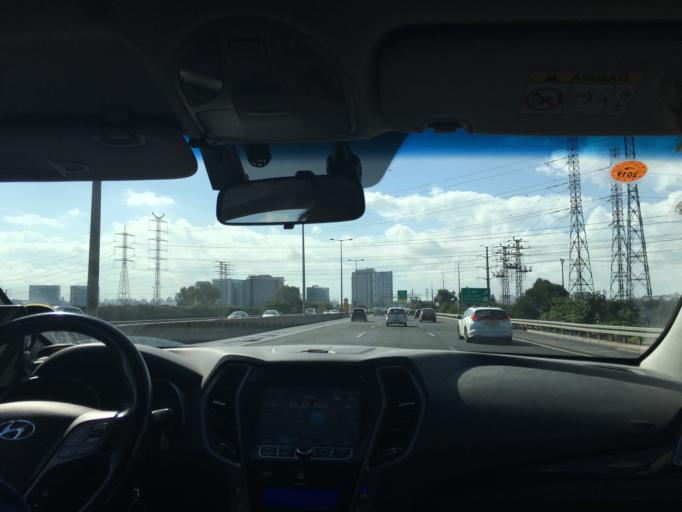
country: IL
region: Tel Aviv
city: Giv`at Shemu'el
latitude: 32.1097
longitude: 34.8499
